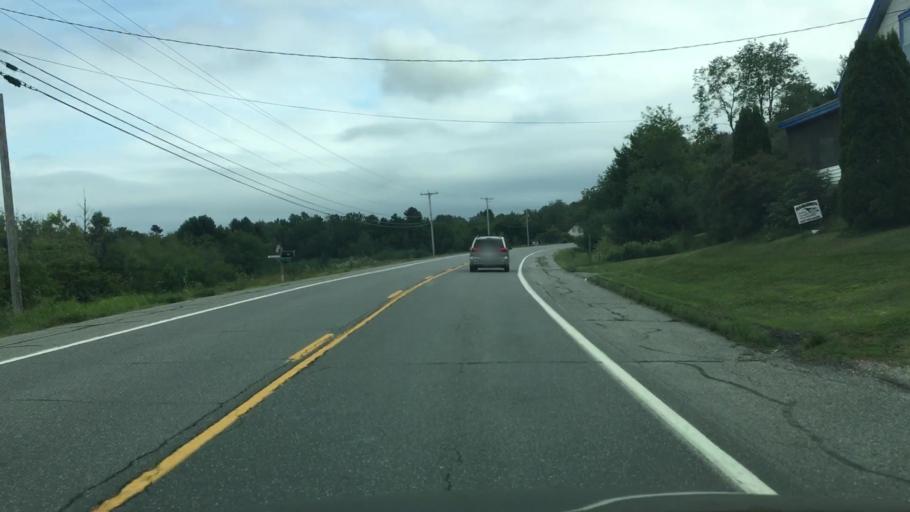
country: US
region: Maine
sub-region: Waldo County
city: Stockton Springs
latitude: 44.5393
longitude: -68.8614
